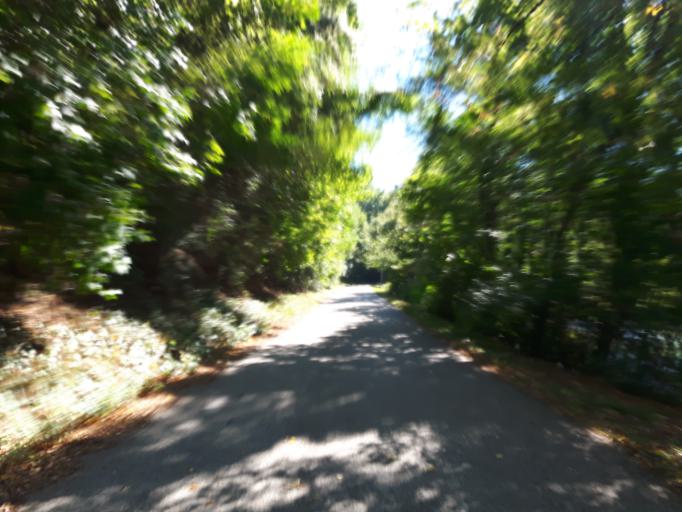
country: DE
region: Baden-Wuerttemberg
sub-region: Regierungsbezirk Stuttgart
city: Zaberfeld
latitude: 49.0509
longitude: 8.9408
